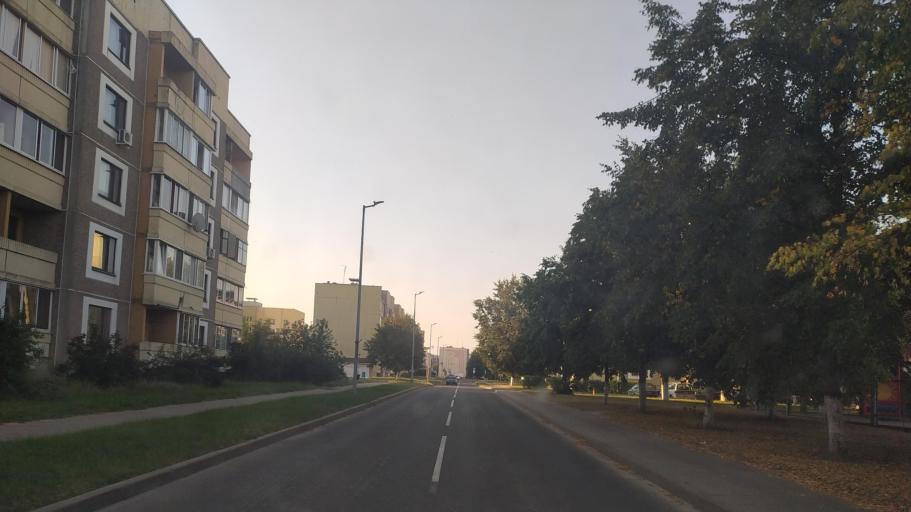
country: BY
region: Brest
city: Byaroza
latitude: 52.5468
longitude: 24.9842
